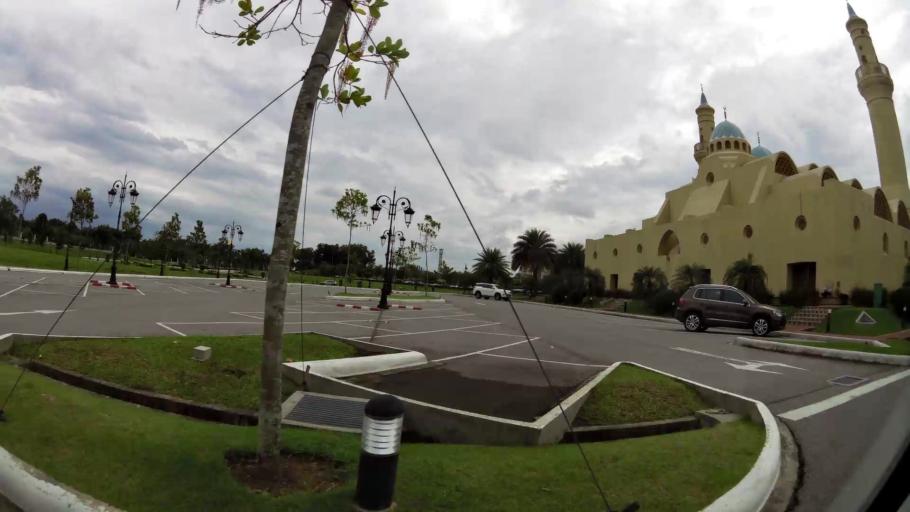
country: BN
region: Brunei and Muara
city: Bandar Seri Begawan
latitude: 4.9179
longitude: 114.9355
